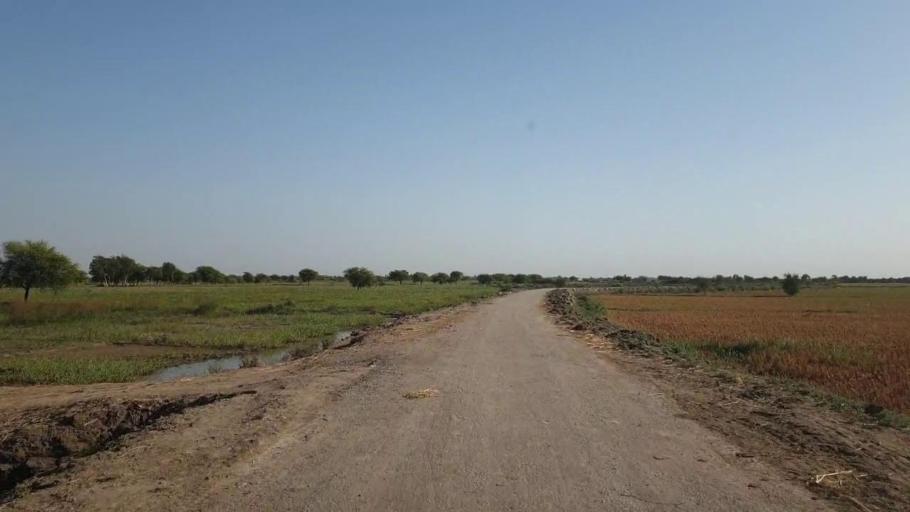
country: PK
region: Sindh
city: Badin
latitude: 24.5976
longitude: 68.9107
